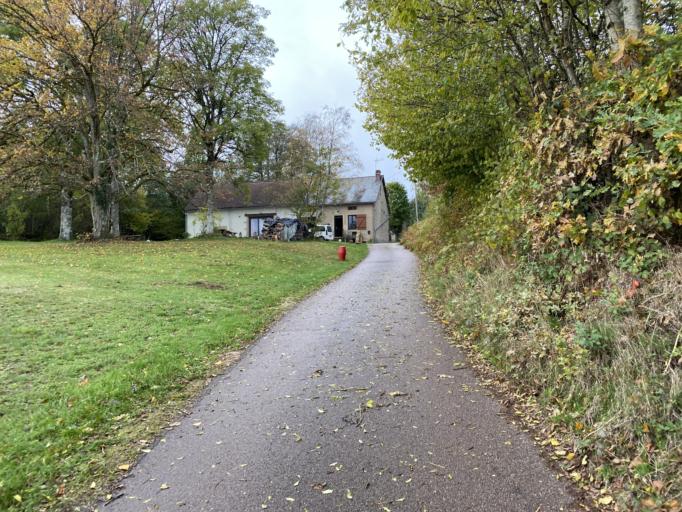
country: FR
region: Bourgogne
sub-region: Departement de la Cote-d'Or
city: Saulieu
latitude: 47.2630
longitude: 4.1700
